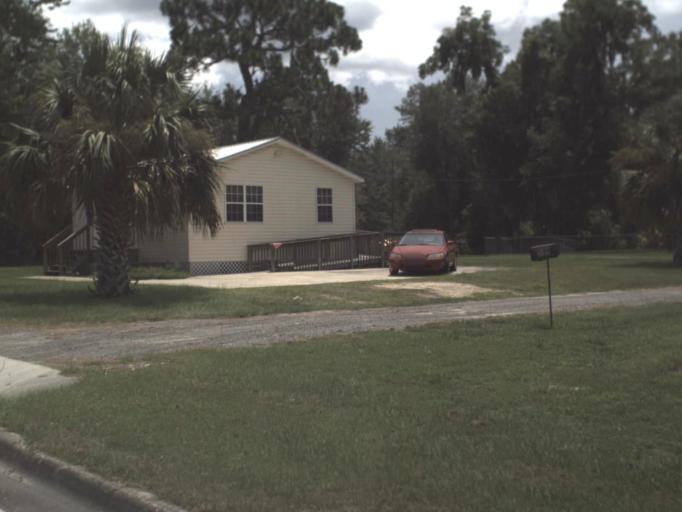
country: US
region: Florida
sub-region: Taylor County
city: Perry
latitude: 30.1100
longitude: -83.5714
